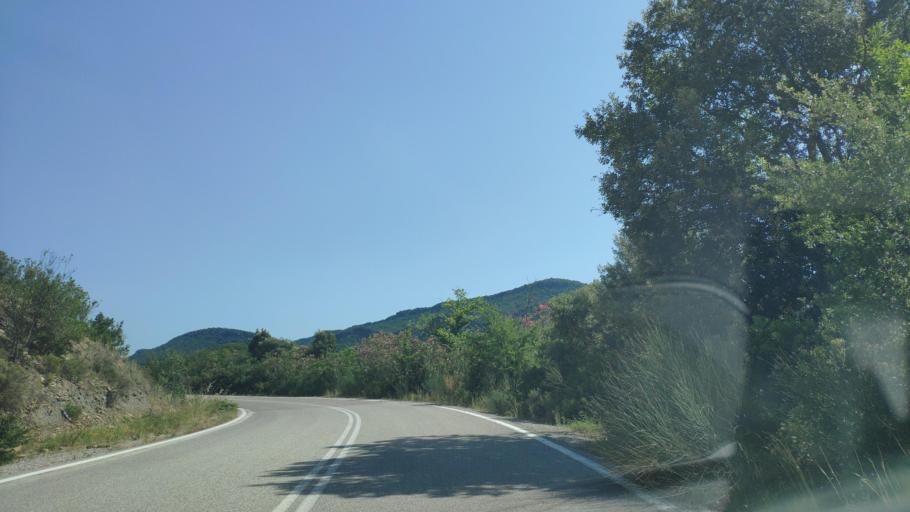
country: GR
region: West Greece
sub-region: Nomos Aitolias kai Akarnanias
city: Lepenou
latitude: 38.7689
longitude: 21.3363
